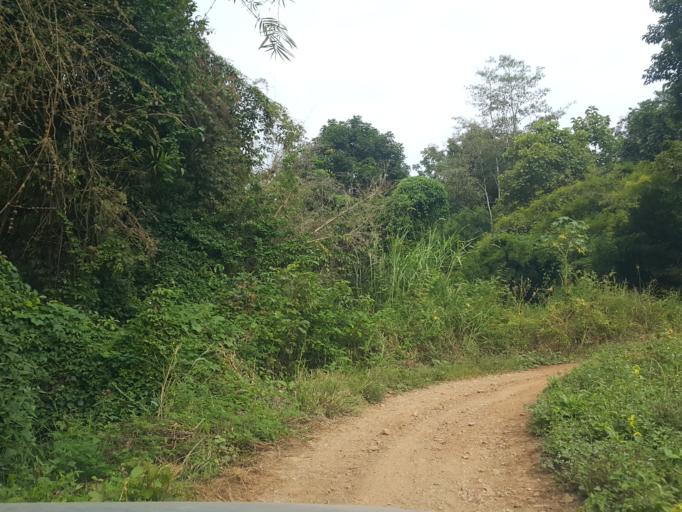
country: TH
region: Mae Hong Son
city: Wiang Nuea
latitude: 19.3955
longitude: 98.4706
